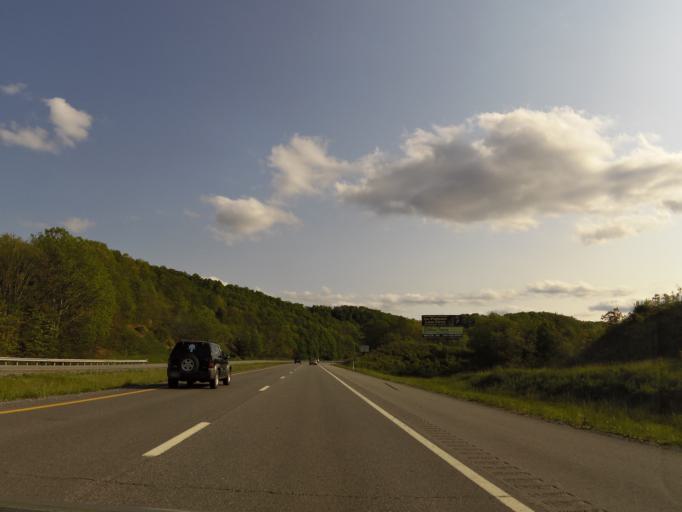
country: US
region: West Virginia
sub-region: Mercer County
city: Princeton
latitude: 37.3082
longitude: -81.1386
